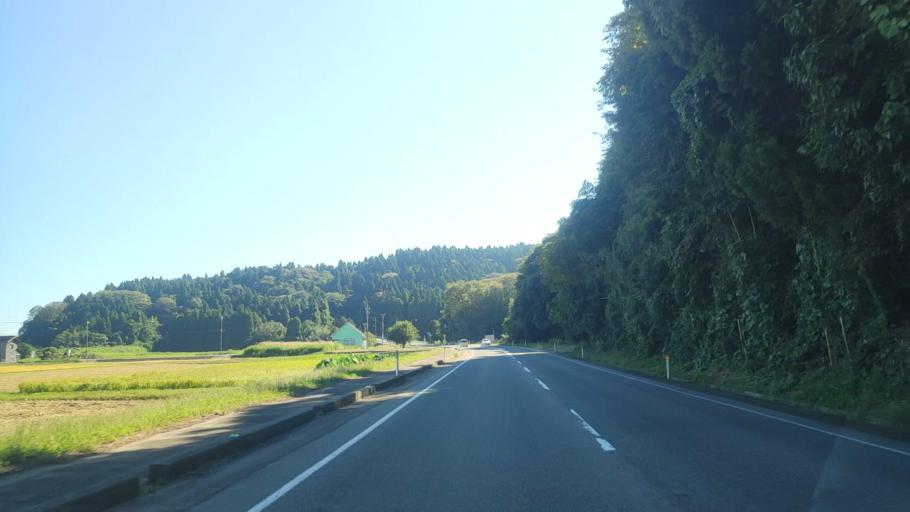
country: JP
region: Ishikawa
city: Nanao
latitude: 37.3886
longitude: 137.2332
